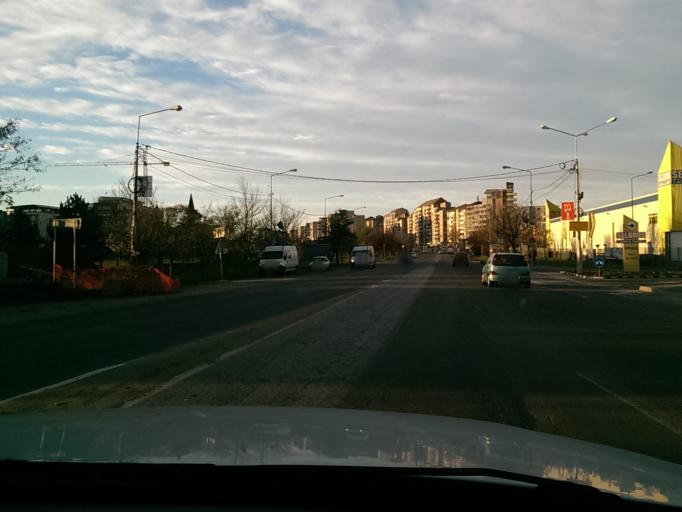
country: RO
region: Bihor
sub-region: Comuna Sanmartin
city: Sanmartin
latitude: 47.0264
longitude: 21.9582
